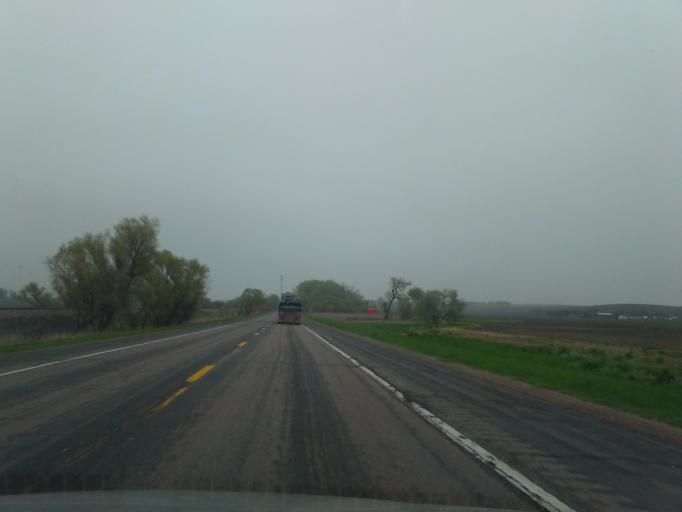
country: US
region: Nebraska
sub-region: Burt County
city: Oakland
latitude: 41.8036
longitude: -96.4804
